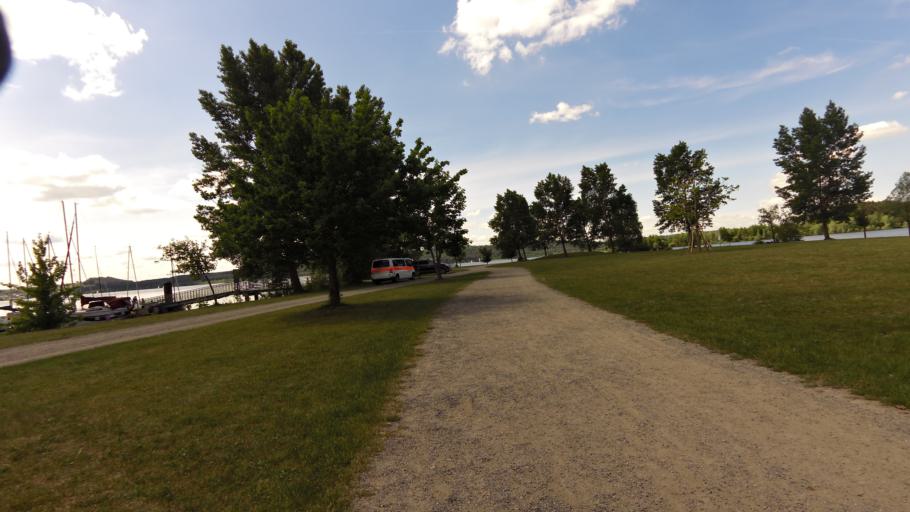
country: DE
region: Bavaria
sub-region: Regierungsbezirk Mittelfranken
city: Spalt
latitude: 49.1430
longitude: 10.9170
